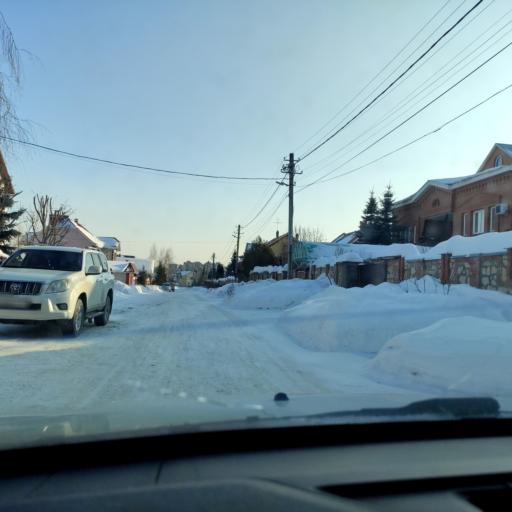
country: RU
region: Samara
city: Novosemeykino
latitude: 53.3230
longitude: 50.2862
